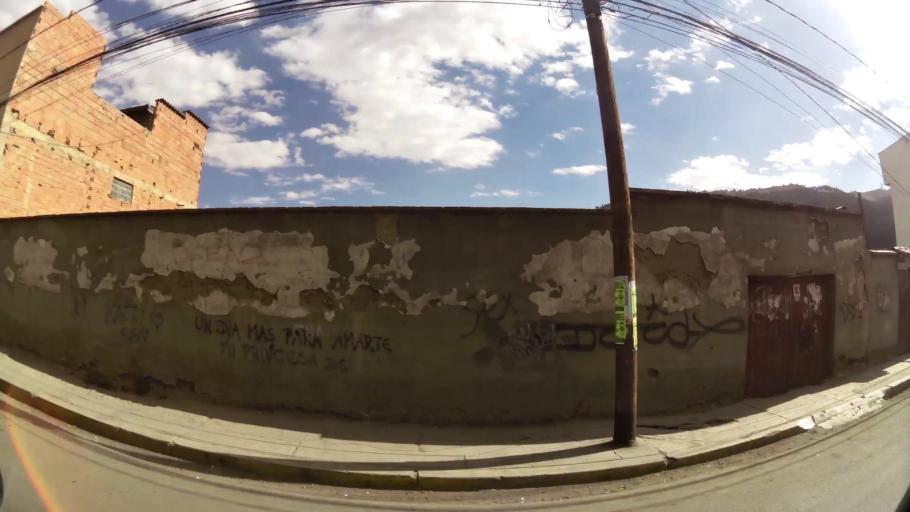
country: BO
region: La Paz
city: La Paz
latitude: -16.4810
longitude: -68.1470
